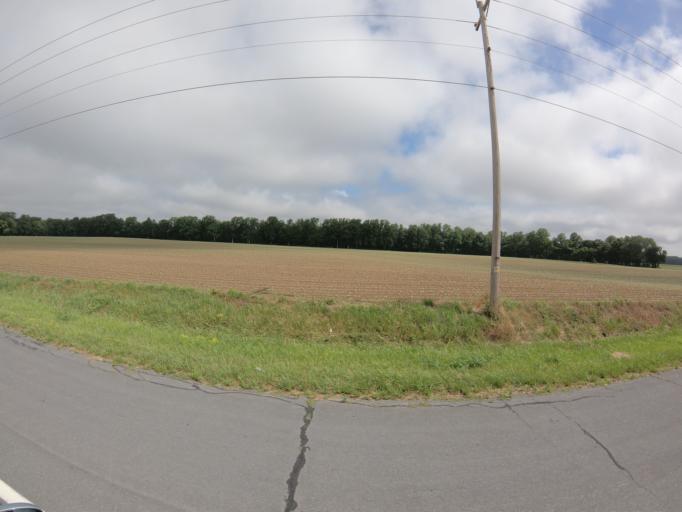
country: US
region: Delaware
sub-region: Kent County
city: Riverview
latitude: 39.0059
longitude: -75.5305
